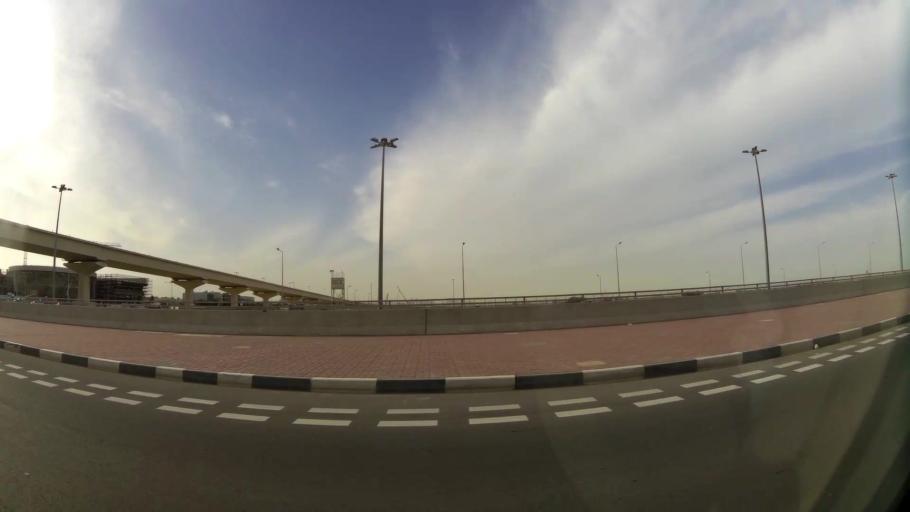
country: QA
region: Al Wakrah
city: Al Wakrah
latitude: 25.2315
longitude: 51.5773
